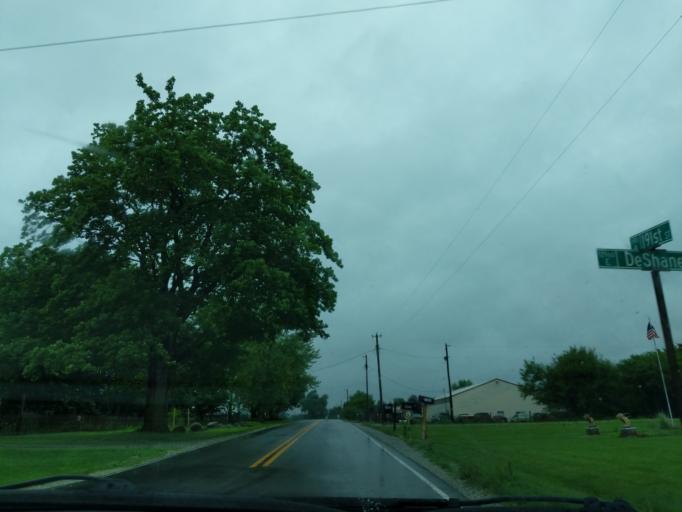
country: US
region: Indiana
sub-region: Hamilton County
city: Noblesville
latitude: 40.0662
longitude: -85.9348
